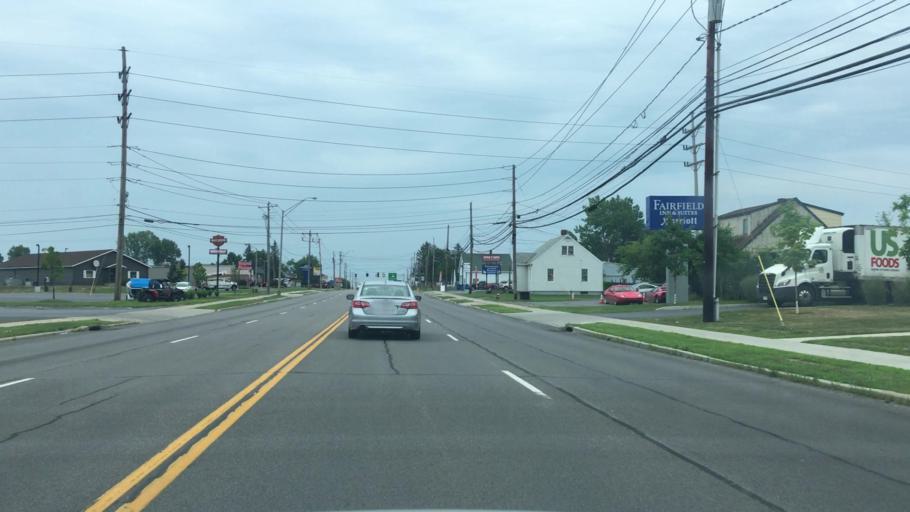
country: US
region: New York
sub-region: Clinton County
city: Plattsburgh West
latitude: 44.6958
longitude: -73.5046
